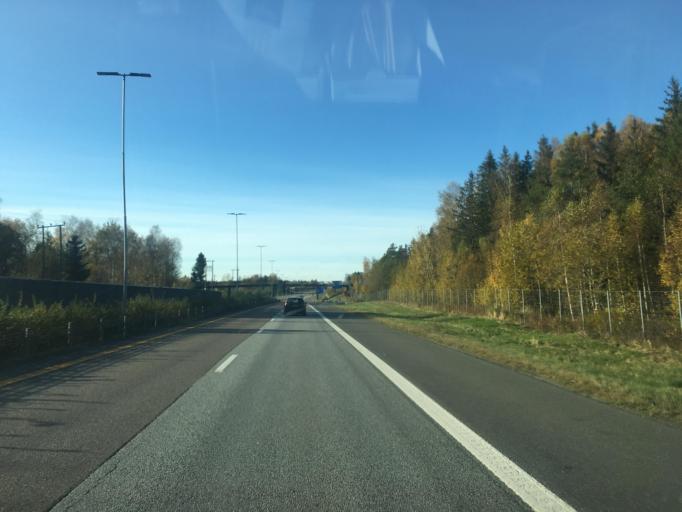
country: NO
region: Ostfold
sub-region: Rade
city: Karlshus
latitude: 59.3560
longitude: 10.8609
